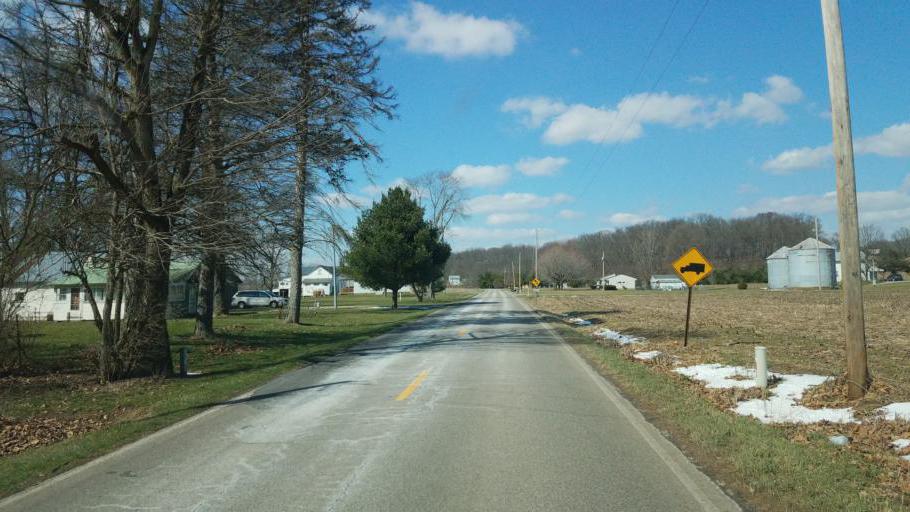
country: US
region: Ohio
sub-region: Knox County
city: Fredericktown
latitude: 40.4453
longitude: -82.5109
